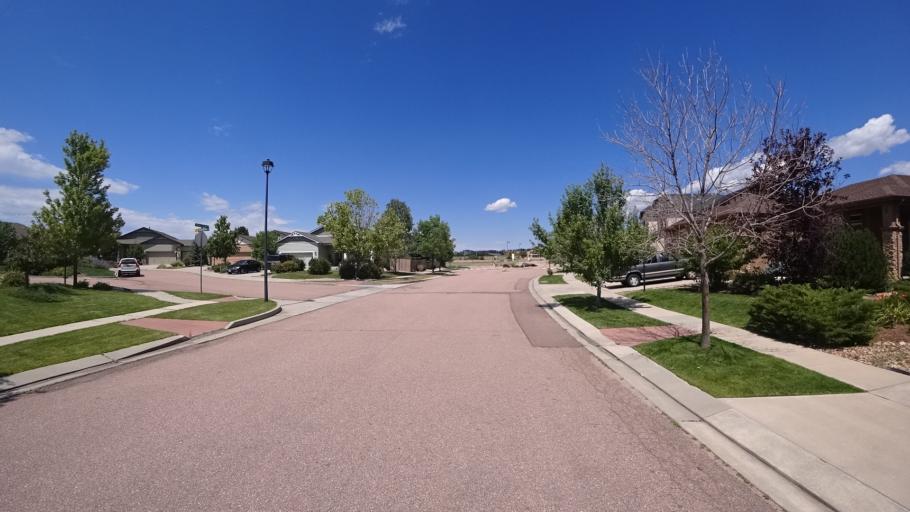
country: US
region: Colorado
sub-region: El Paso County
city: Black Forest
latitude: 38.9715
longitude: -104.7540
